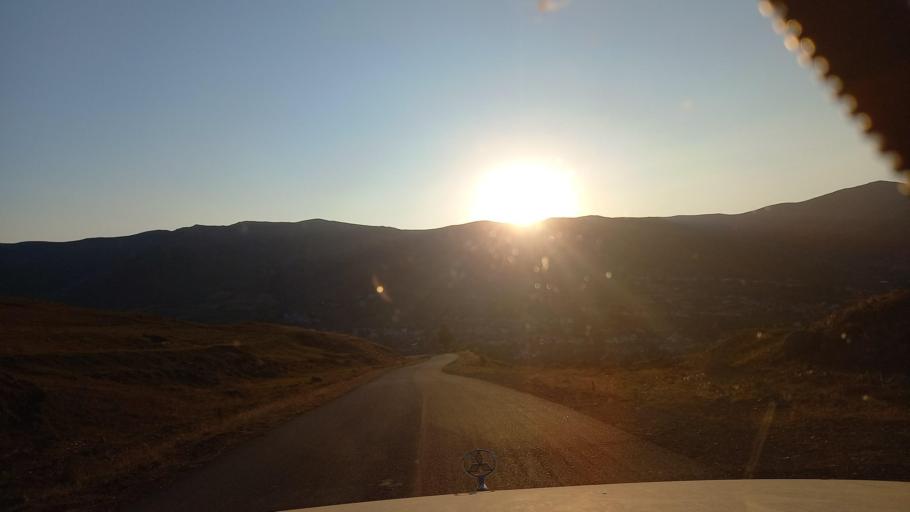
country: AZ
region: Gadabay Rayon
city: Ariqdam
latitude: 40.6836
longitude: 45.7758
